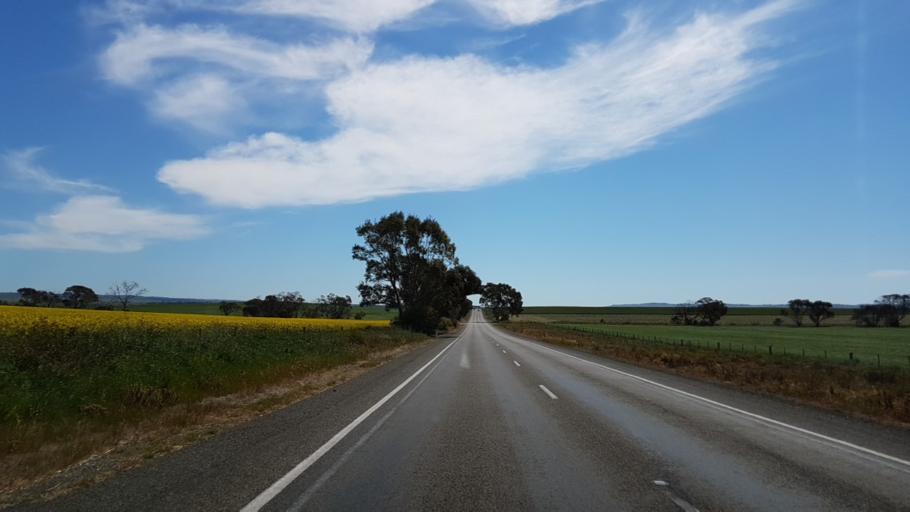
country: AU
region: South Australia
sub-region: Light
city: Freeling
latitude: -34.3970
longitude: 138.7530
